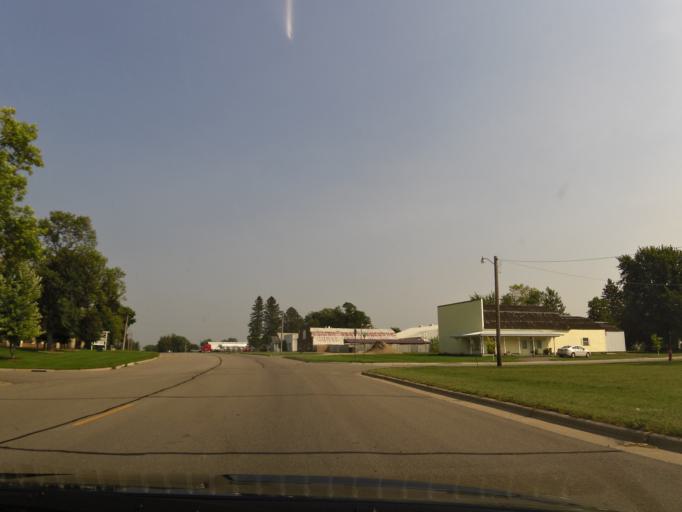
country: US
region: Minnesota
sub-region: Grant County
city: Elbow Lake
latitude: 45.9923
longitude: -95.9642
